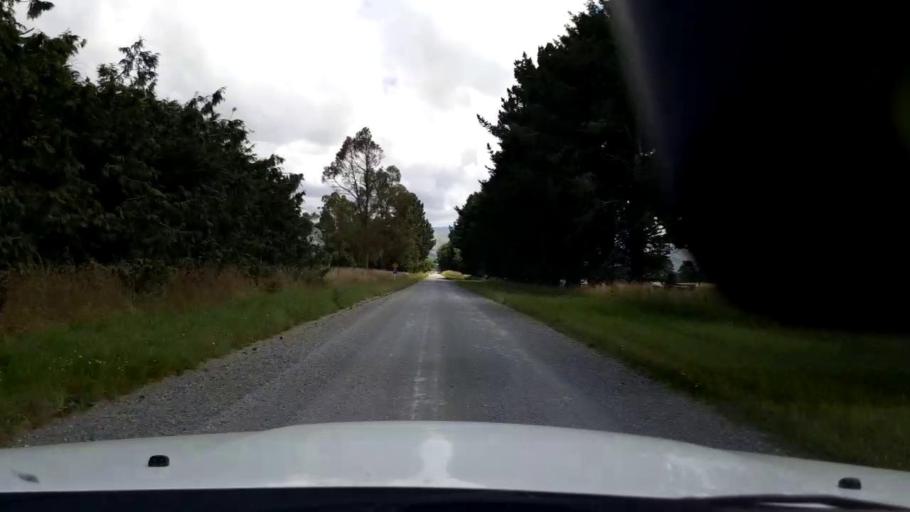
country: NZ
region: Canterbury
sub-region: Timaru District
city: Pleasant Point
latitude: -43.9768
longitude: 171.2685
